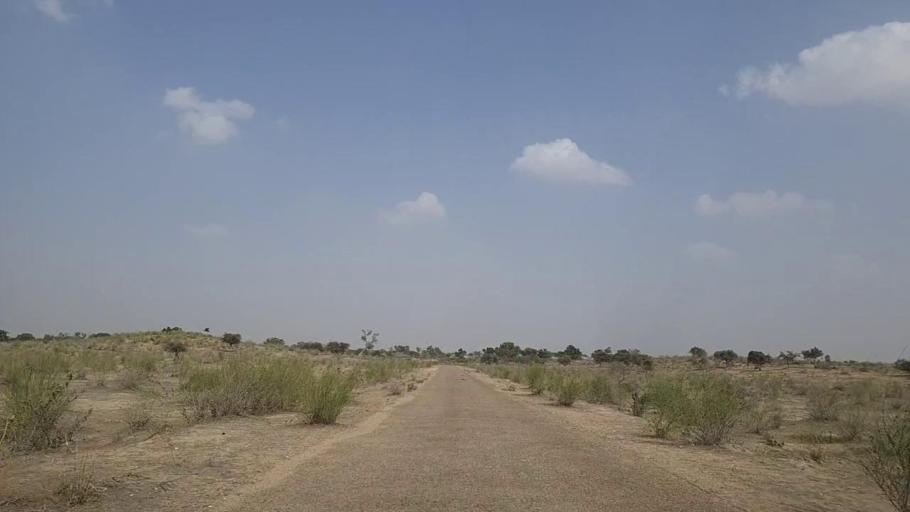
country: PK
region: Sindh
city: Islamkot
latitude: 24.7883
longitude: 70.0795
